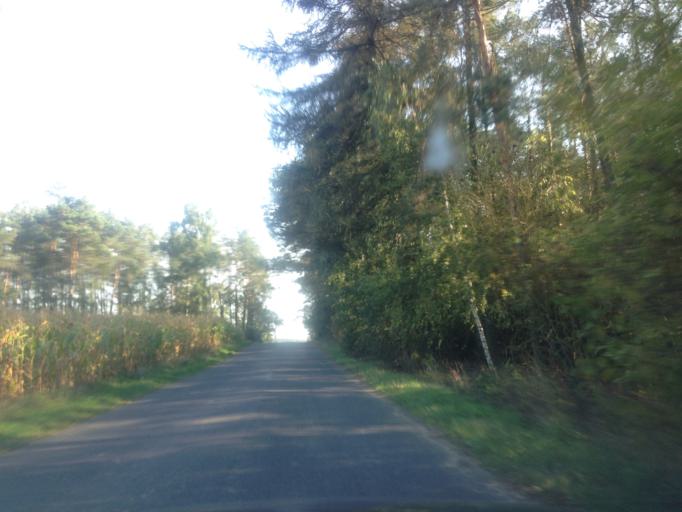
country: PL
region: Kujawsko-Pomorskie
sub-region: Powiat brodnicki
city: Brzozie
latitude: 53.2994
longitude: 19.6862
